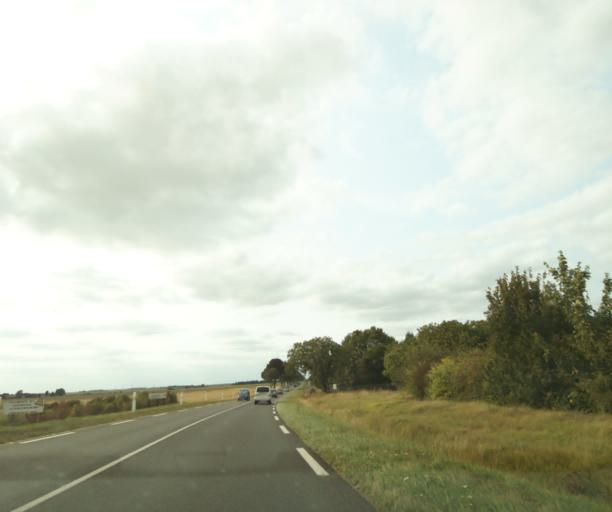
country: FR
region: Centre
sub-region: Departement d'Indre-et-Loire
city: Reignac-sur-Indre
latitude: 47.1969
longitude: 0.9180
